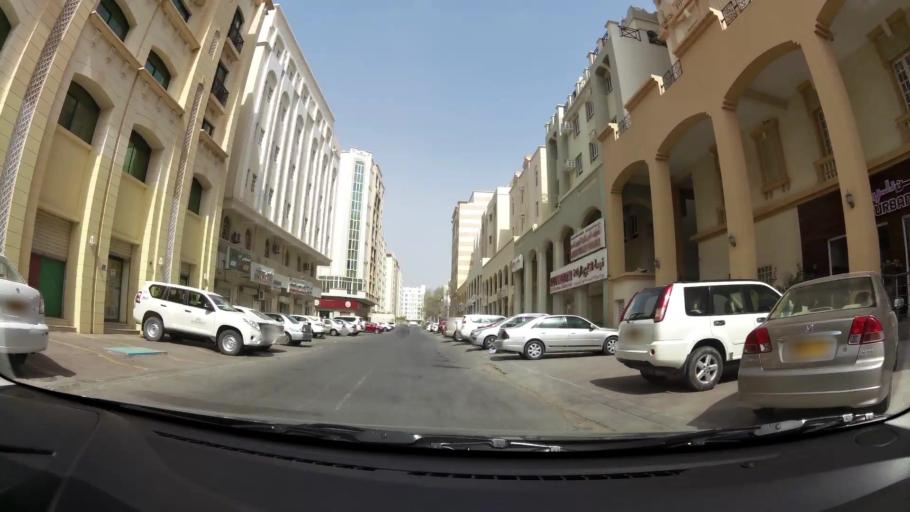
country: OM
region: Muhafazat Masqat
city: Bawshar
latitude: 23.5813
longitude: 58.3959
